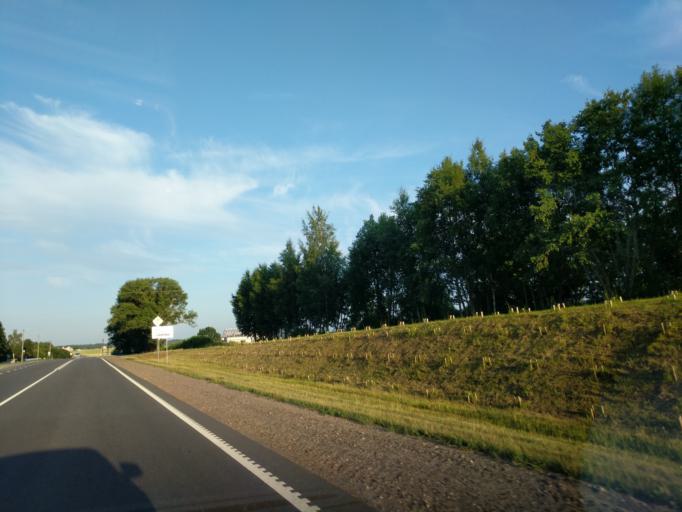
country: BY
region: Minsk
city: Syomkava
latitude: 54.1030
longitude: 27.4760
